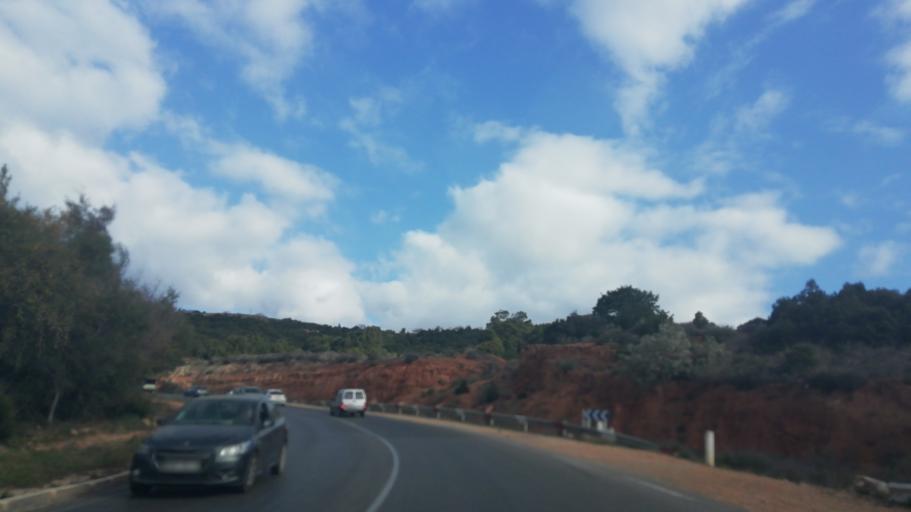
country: DZ
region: Relizane
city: Mazouna
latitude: 36.2386
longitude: 0.5427
